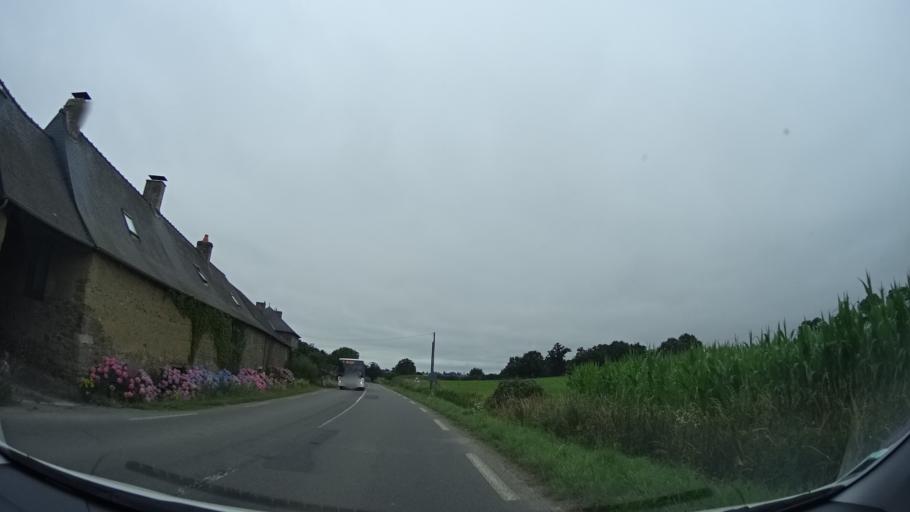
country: FR
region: Brittany
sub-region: Departement d'Ille-et-Vilaine
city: Irodouer
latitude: 48.3017
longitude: -1.9405
